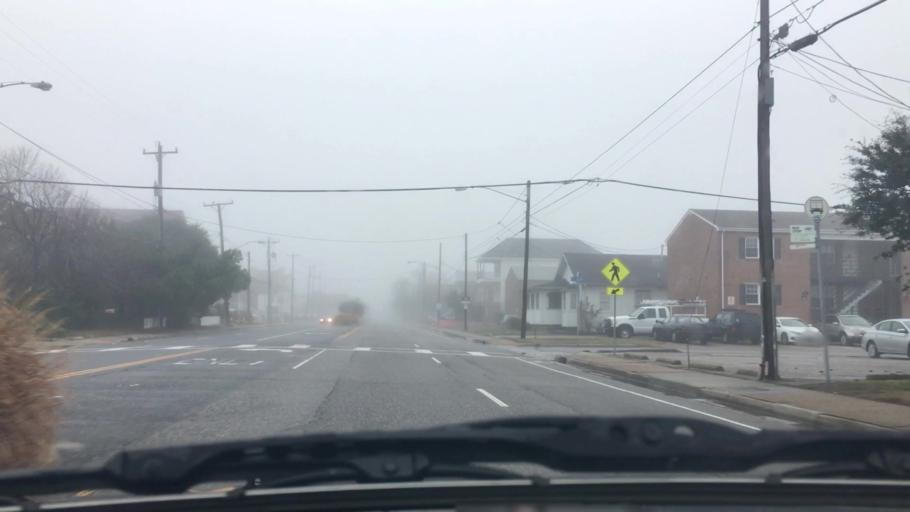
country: US
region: Virginia
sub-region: City of Hampton
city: East Hampton
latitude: 36.9662
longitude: -76.2755
